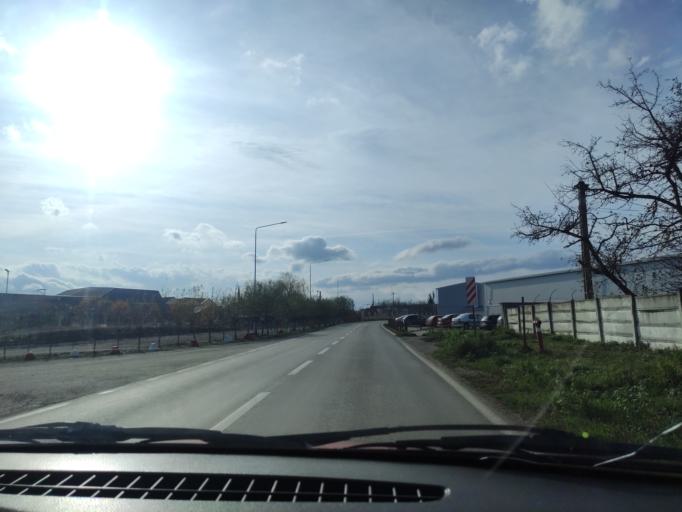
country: RO
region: Brasov
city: Codlea
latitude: 45.7067
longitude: 25.4595
